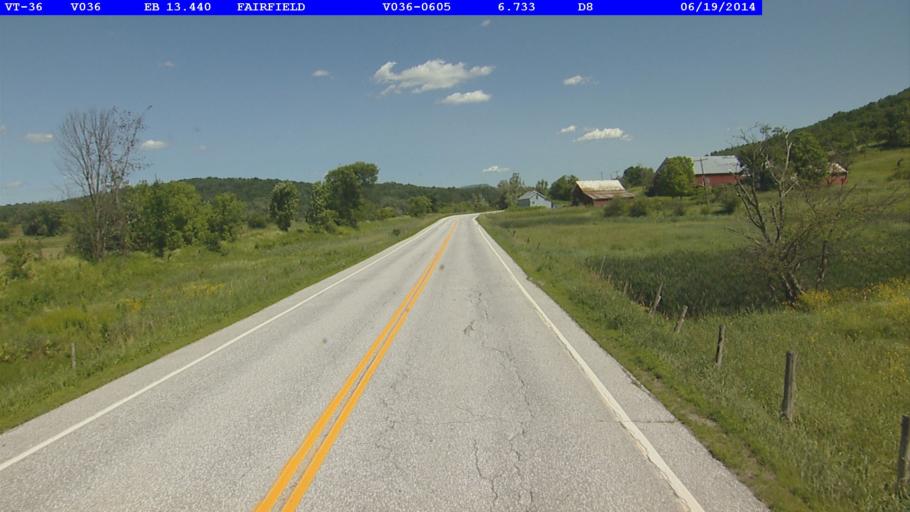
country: US
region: Vermont
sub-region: Franklin County
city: Enosburg Falls
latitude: 44.8069
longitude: -72.9015
